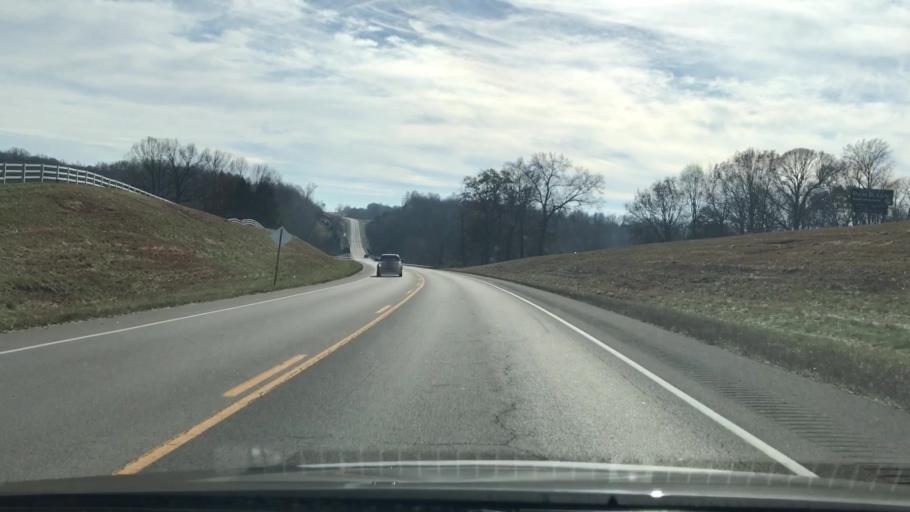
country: US
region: Kentucky
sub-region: Monroe County
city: Tompkinsville
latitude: 36.7514
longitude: -85.6913
